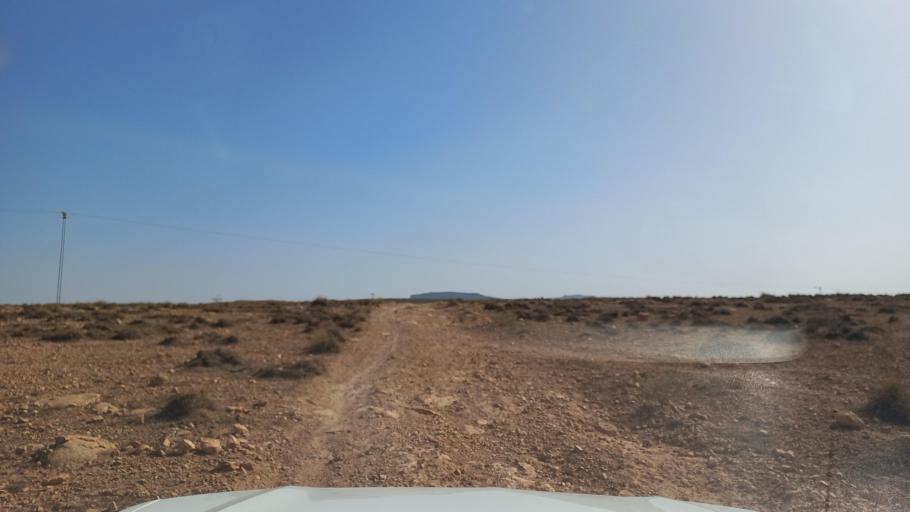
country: TN
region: Al Qasrayn
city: Kasserine
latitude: 35.2072
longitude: 8.9728
